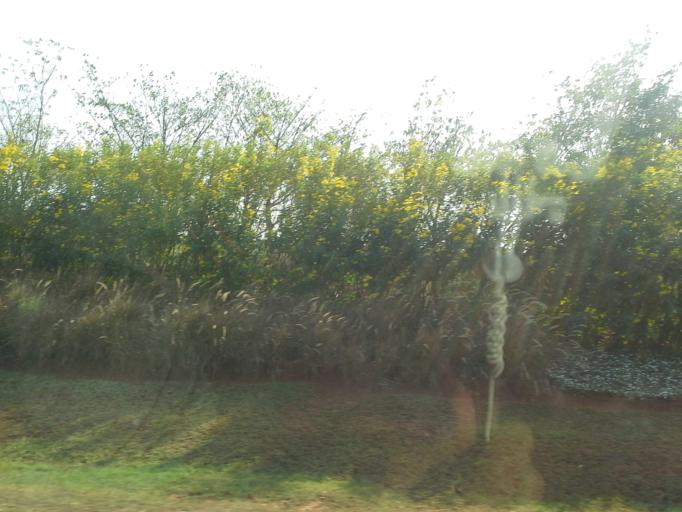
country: IN
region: Telangana
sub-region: Rangareddi
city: Balapur
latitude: 17.2442
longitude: 78.4055
